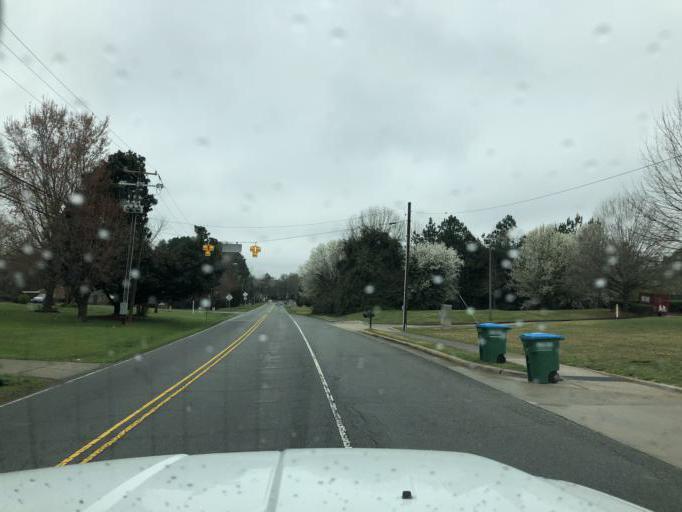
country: US
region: North Carolina
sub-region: Gaston County
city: Mount Holly
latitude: 35.3150
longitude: -80.9646
